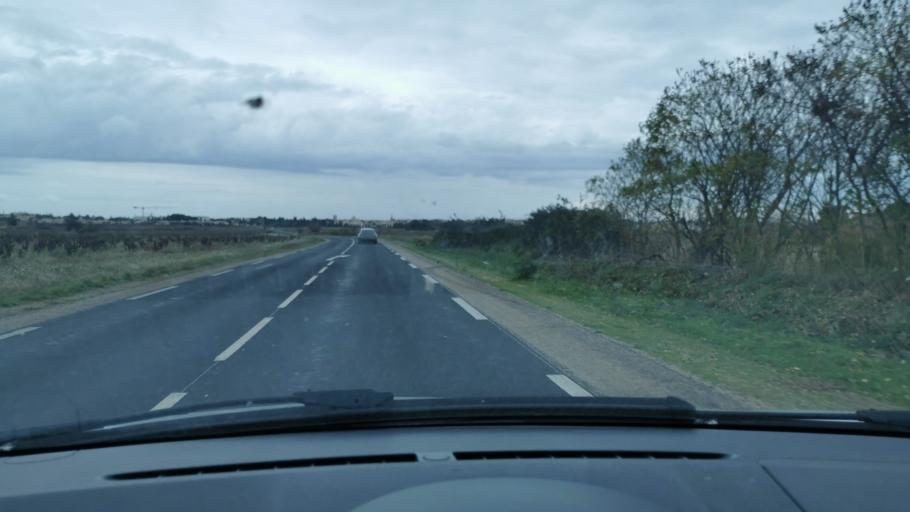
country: FR
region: Languedoc-Roussillon
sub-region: Departement de l'Herault
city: Frontignan
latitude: 43.4479
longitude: 3.7298
